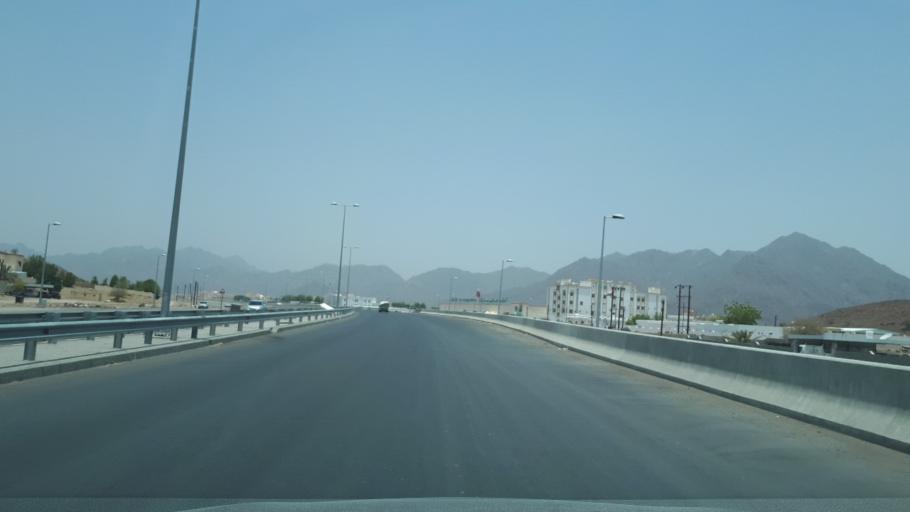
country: OM
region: Al Batinah
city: Rustaq
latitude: 23.4360
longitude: 57.4192
